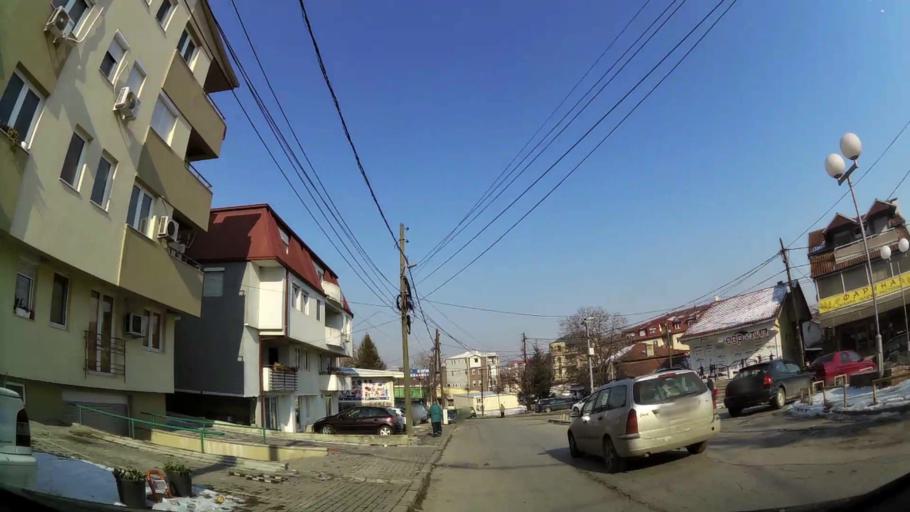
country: MK
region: Karpos
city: Skopje
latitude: 41.9753
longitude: 21.4384
